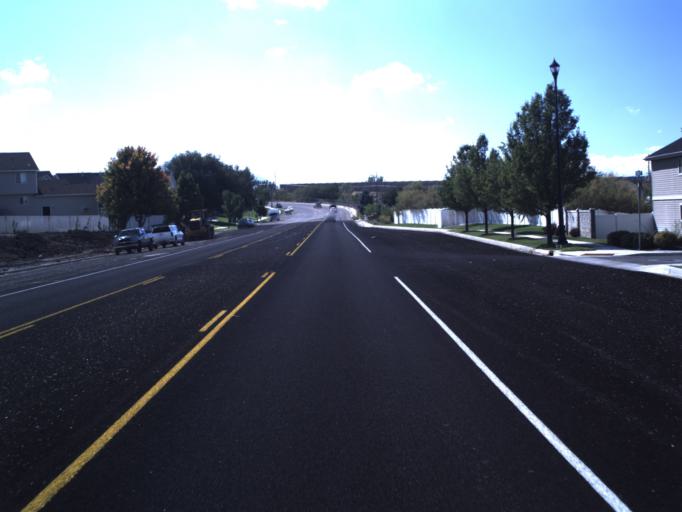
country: US
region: Utah
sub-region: Utah County
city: Spanish Fork
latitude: 40.1188
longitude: -111.6329
